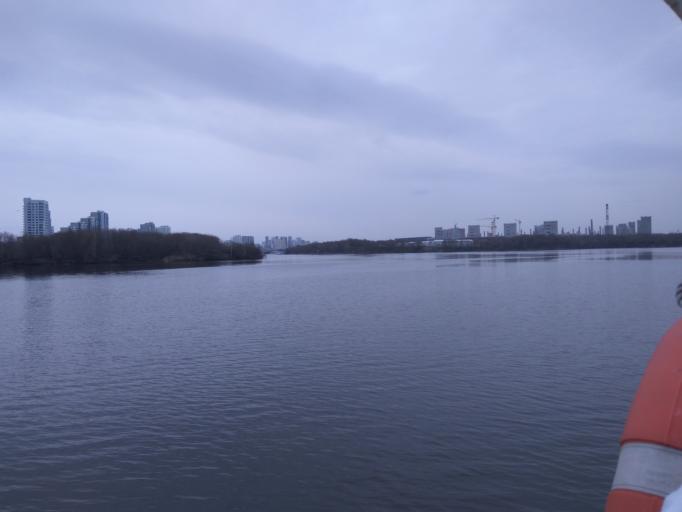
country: RU
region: Moskovskaya
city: Kozhukhovo
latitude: 55.6948
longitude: 37.6949
